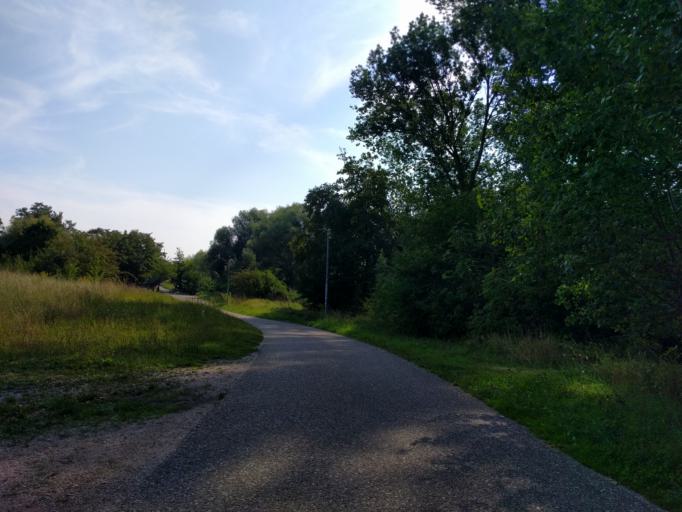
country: DE
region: Bavaria
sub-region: Upper Palatinate
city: Regensburg
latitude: 49.0238
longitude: 12.1322
